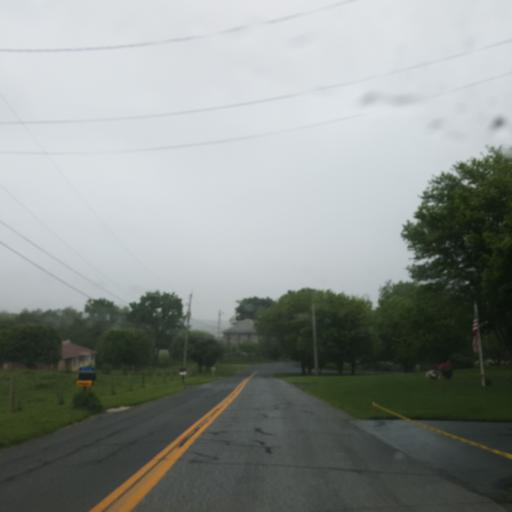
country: US
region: Pennsylvania
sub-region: Lebanon County
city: Palmyra
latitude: 40.4088
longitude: -76.5934
